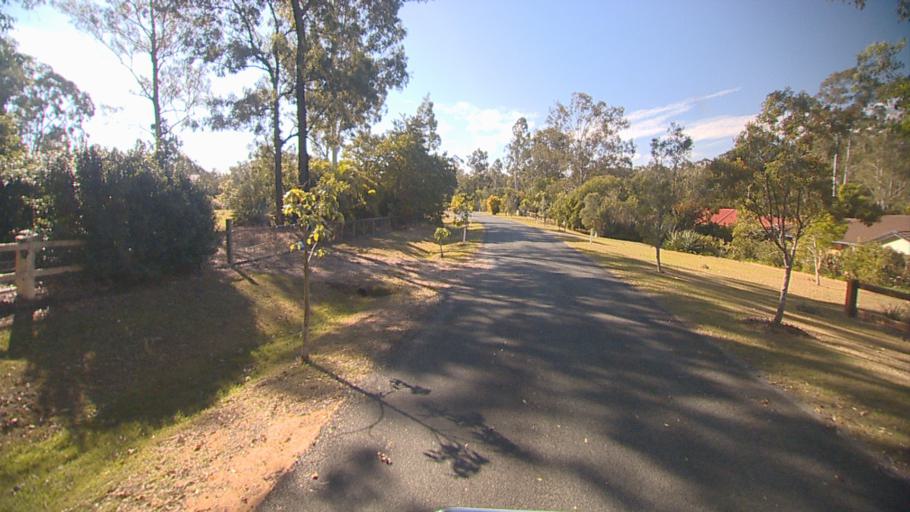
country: AU
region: Queensland
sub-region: Ipswich
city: Springfield Lakes
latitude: -27.7298
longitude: 152.9293
